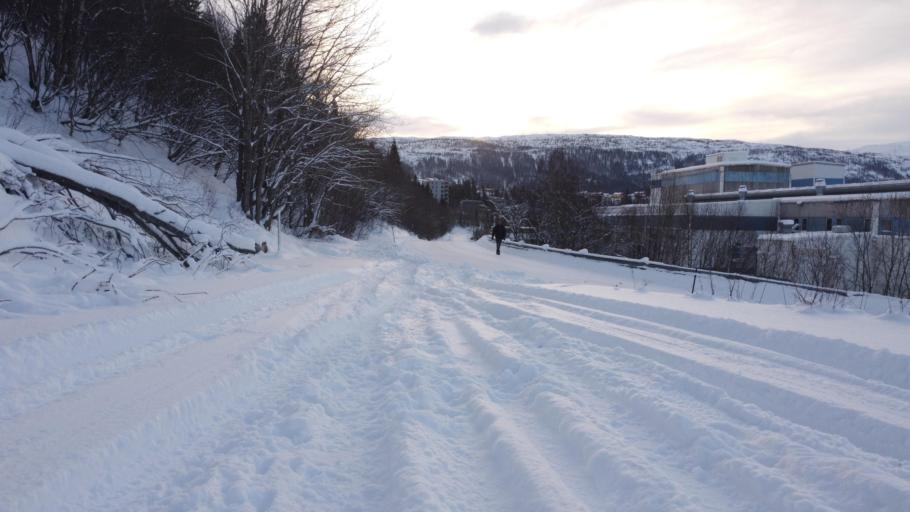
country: NO
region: Nordland
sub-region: Rana
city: Mo i Rana
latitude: 66.3241
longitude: 14.1542
